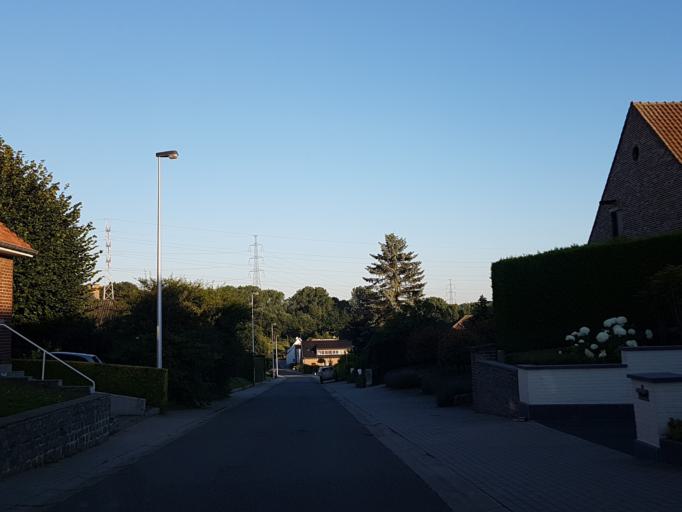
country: BE
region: Flanders
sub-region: Provincie Vlaams-Brabant
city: Asse
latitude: 50.8770
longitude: 4.2264
